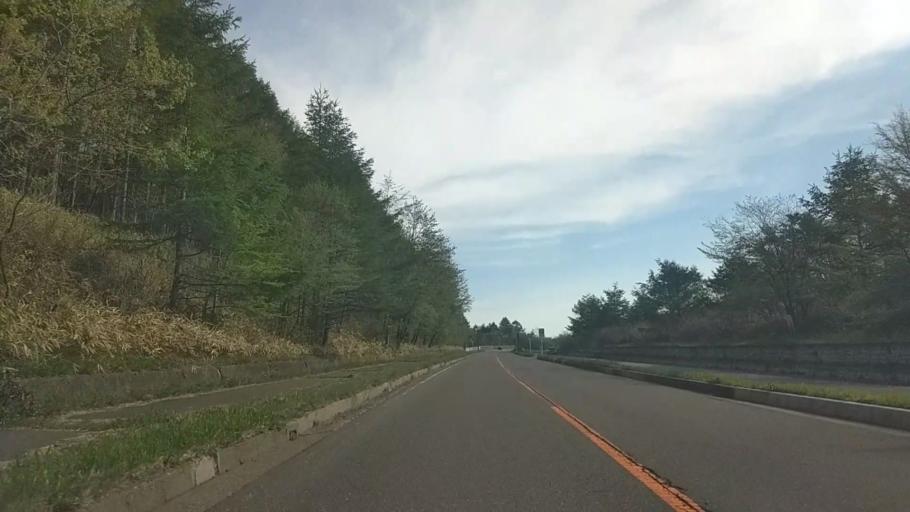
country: JP
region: Yamanashi
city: Nirasaki
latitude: 35.9411
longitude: 138.4498
